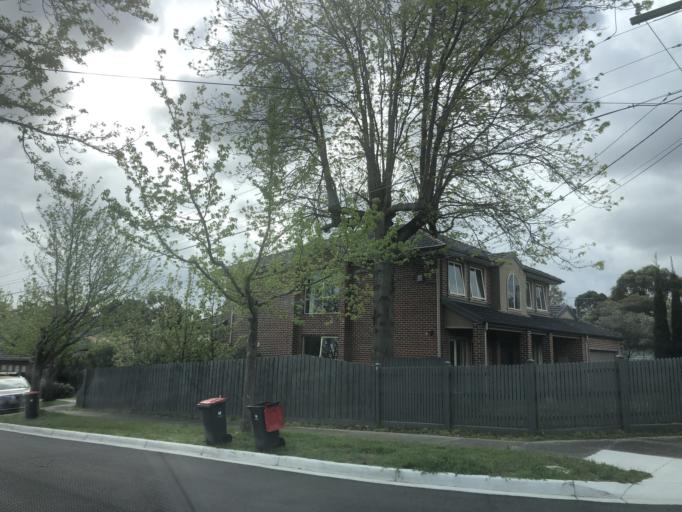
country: AU
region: Victoria
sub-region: Monash
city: Ashwood
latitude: -37.8810
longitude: 145.1186
